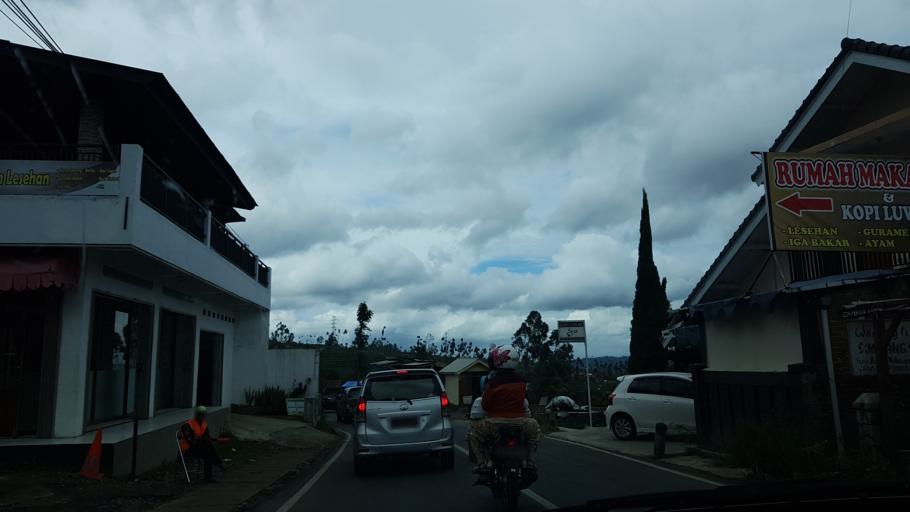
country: ID
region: West Java
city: Banjar
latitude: -7.1229
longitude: 107.4329
